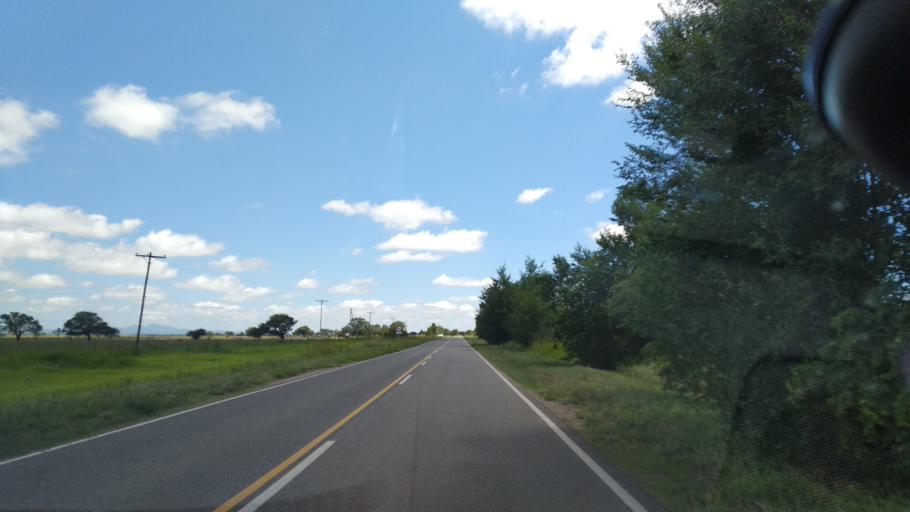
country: AR
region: Cordoba
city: Villa Cura Brochero
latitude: -31.5997
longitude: -65.1109
